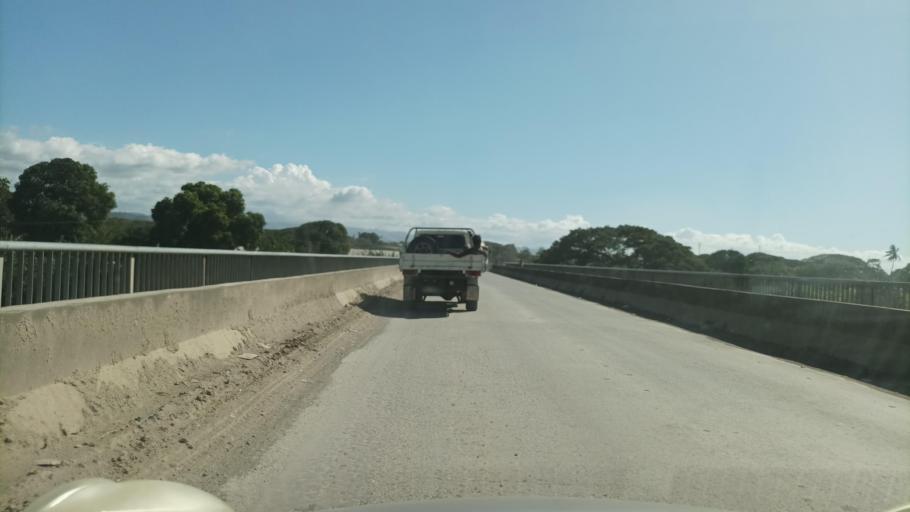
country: SB
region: Guadalcanal
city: Honiara
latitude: -9.4284
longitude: 160.0288
